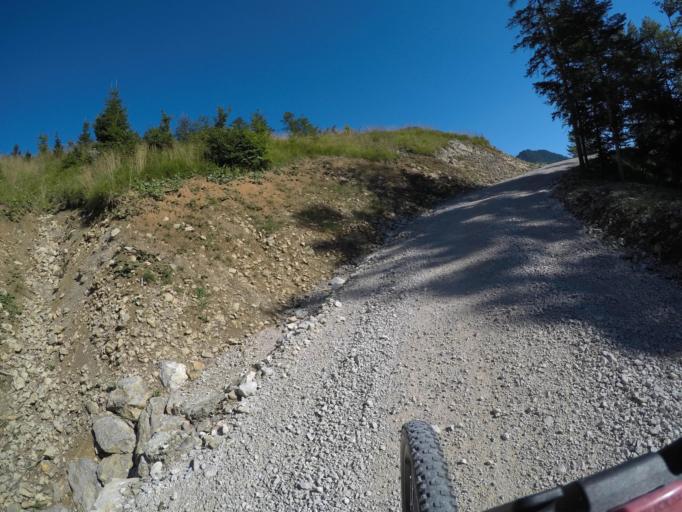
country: IT
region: Friuli Venezia Giulia
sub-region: Provincia di Udine
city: Malborghetto
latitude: 46.4575
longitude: 13.4561
